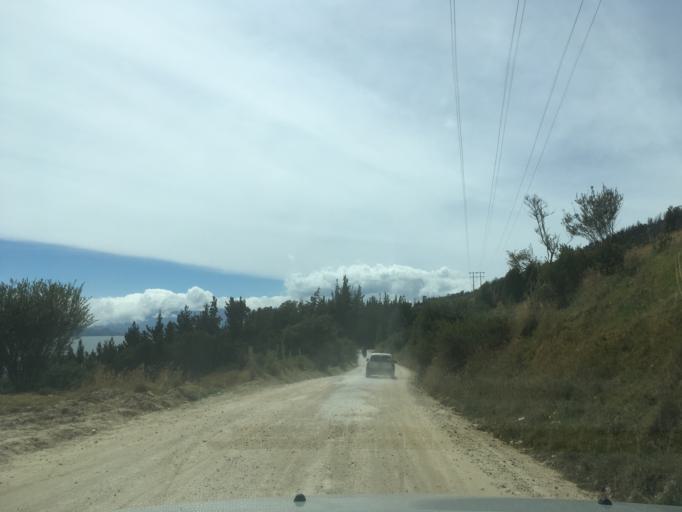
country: CO
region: Boyaca
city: Aquitania
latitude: 5.5937
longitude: -72.9184
